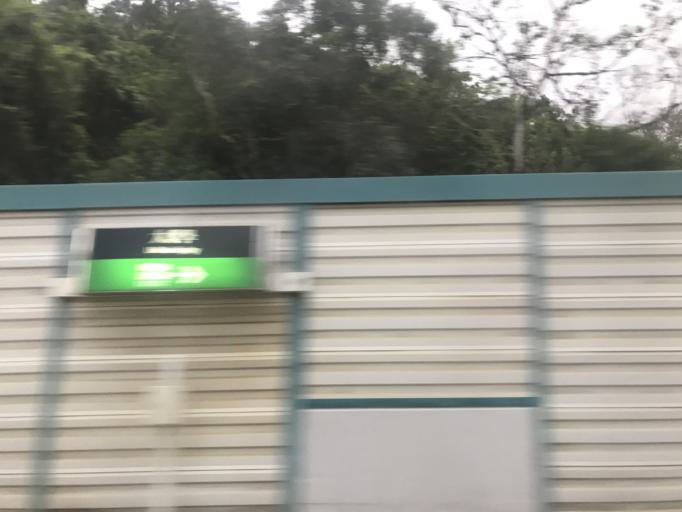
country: HK
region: Sha Tin
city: Sha Tin
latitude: 22.4127
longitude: 114.2100
